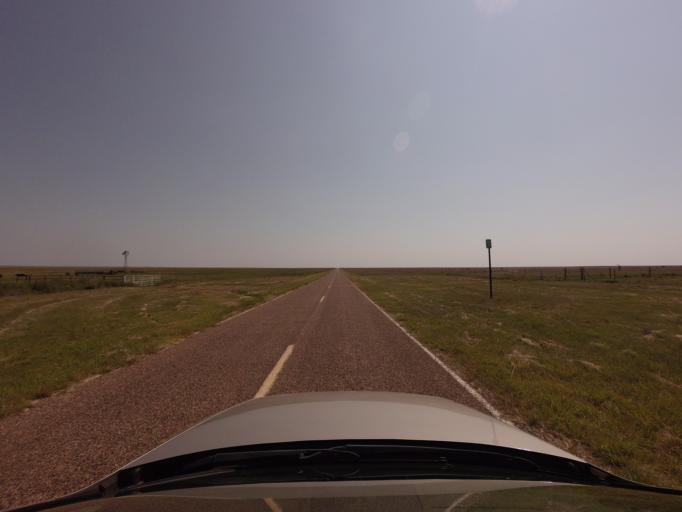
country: US
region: New Mexico
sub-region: Curry County
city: Cannon Air Force Base
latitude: 34.6334
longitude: -103.4781
